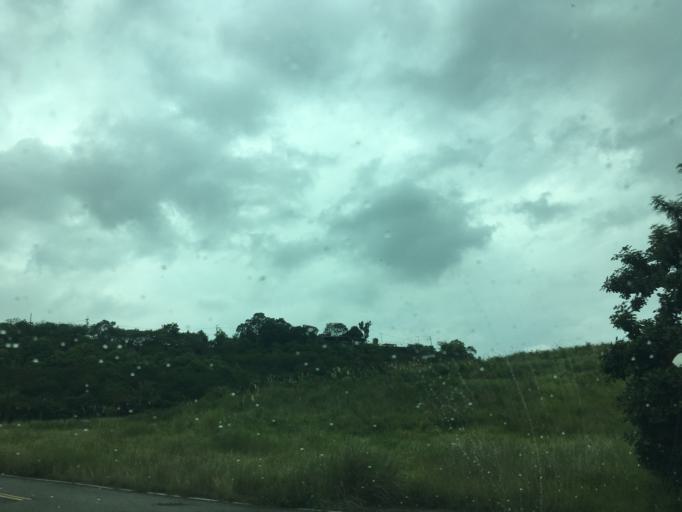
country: TW
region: Taiwan
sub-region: Taichung City
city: Taichung
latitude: 24.0566
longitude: 120.7243
